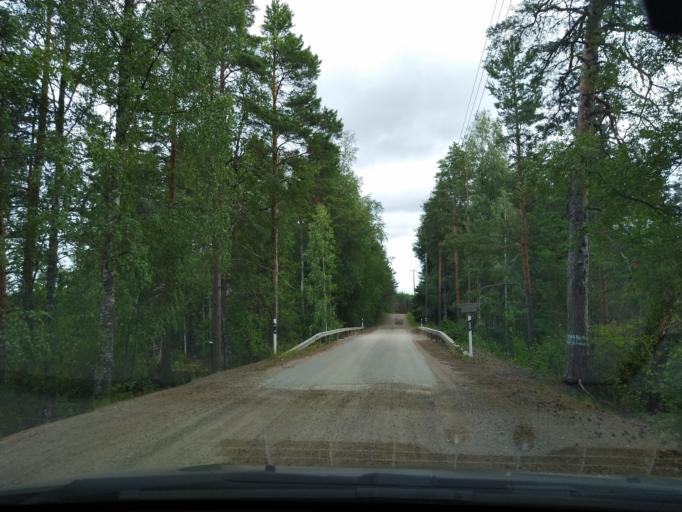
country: FI
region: Southern Savonia
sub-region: Mikkeli
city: Maentyharju
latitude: 61.1383
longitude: 26.8870
